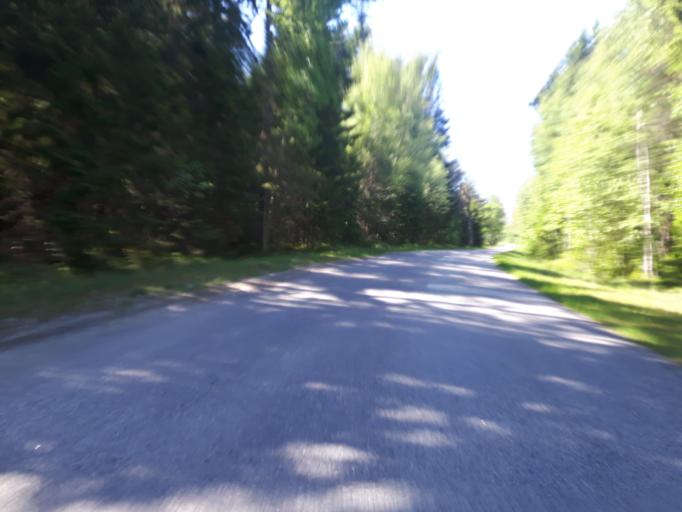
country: EE
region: Laeaene-Virumaa
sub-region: Viru-Nigula vald
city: Kunda
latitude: 59.5480
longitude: 26.3898
